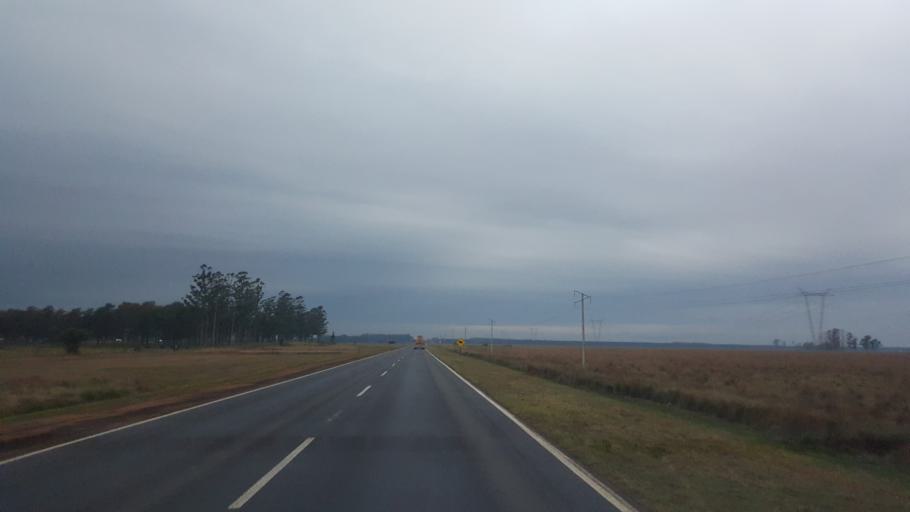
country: AR
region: Corrientes
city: Ituzaingo
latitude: -27.5967
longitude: -56.4653
